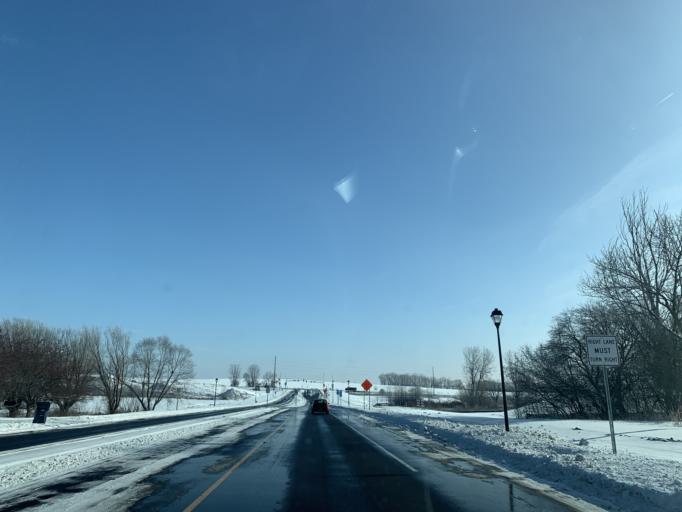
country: US
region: Minnesota
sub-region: Dakota County
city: Lakeville
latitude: 44.6560
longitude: -93.2228
